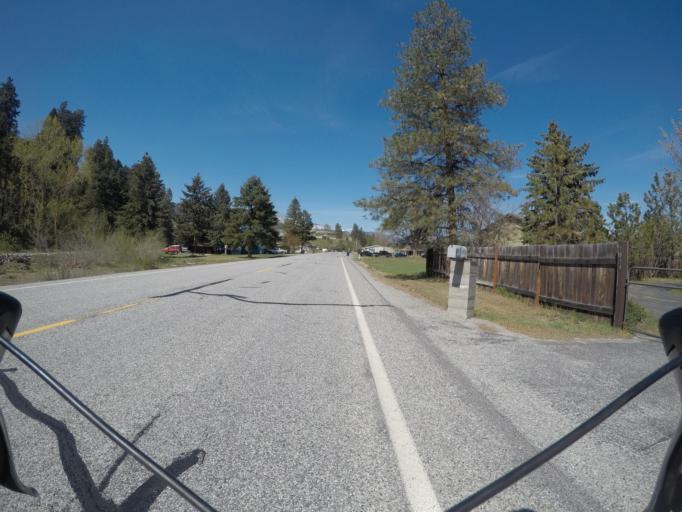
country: US
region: Washington
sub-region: Chelan County
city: Cashmere
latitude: 47.5306
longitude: -120.5443
